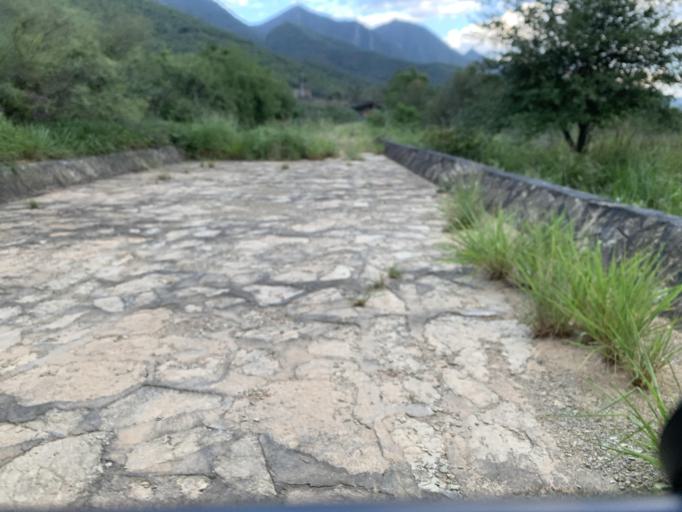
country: MX
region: Nuevo Leon
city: Santiago
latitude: 25.5060
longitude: -100.1804
